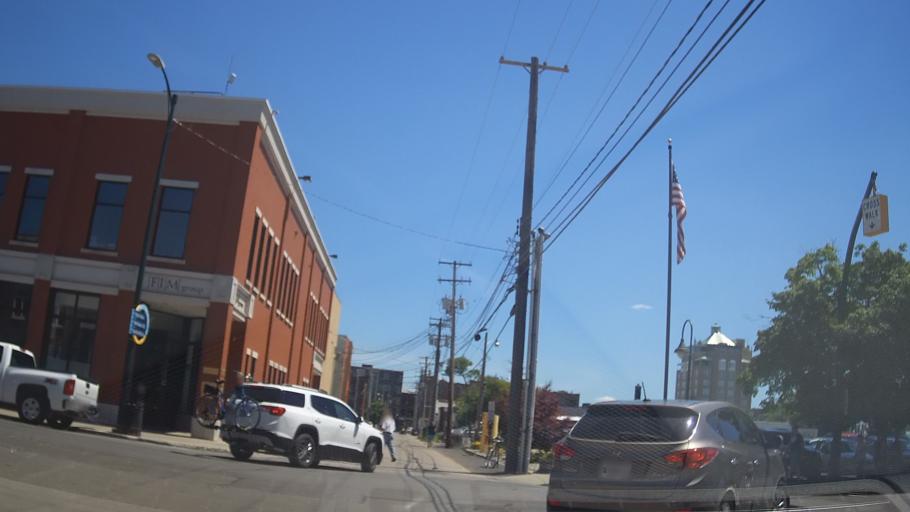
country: US
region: Michigan
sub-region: Grand Traverse County
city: Traverse City
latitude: 44.7635
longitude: -85.6212
